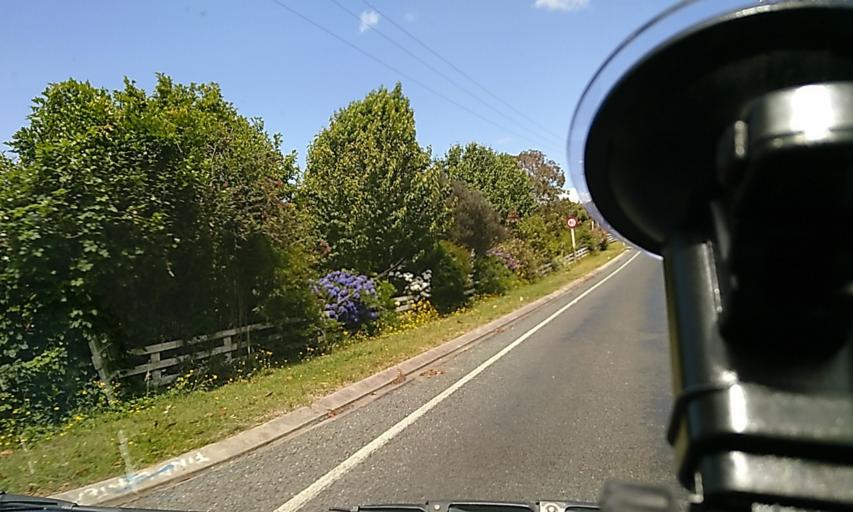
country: NZ
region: Bay of Plenty
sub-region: Western Bay of Plenty District
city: Waihi Beach
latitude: -37.4470
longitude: 175.9566
